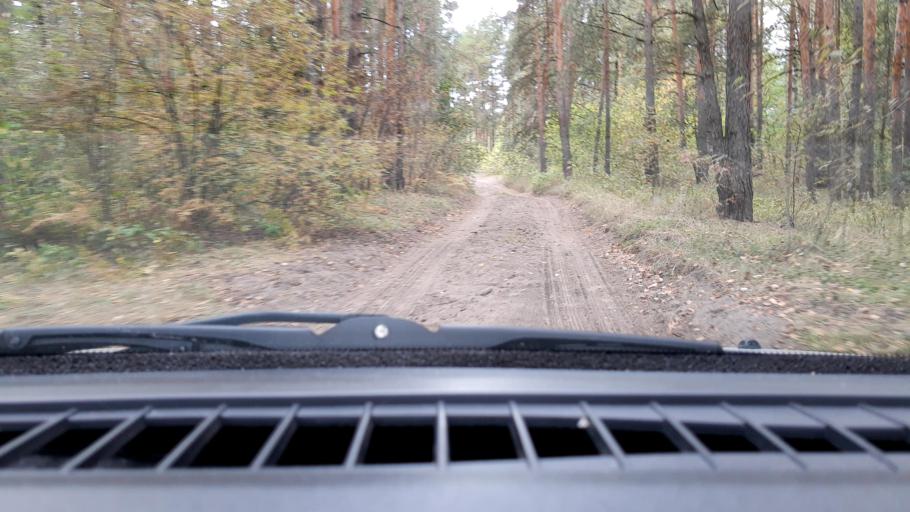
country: RU
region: Nizjnij Novgorod
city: Gorbatovka
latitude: 56.3102
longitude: 43.7190
